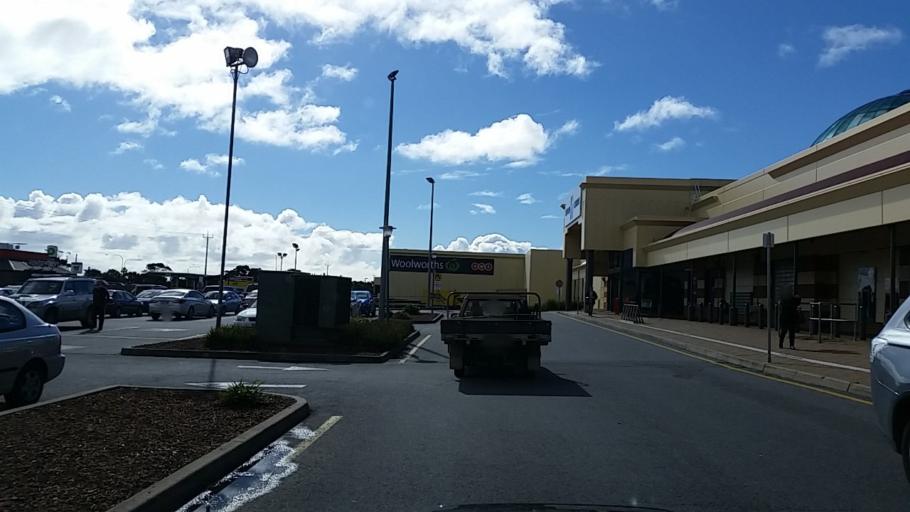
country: AU
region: South Australia
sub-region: Onkaparinga
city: Seaford
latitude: -35.1899
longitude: 138.4787
